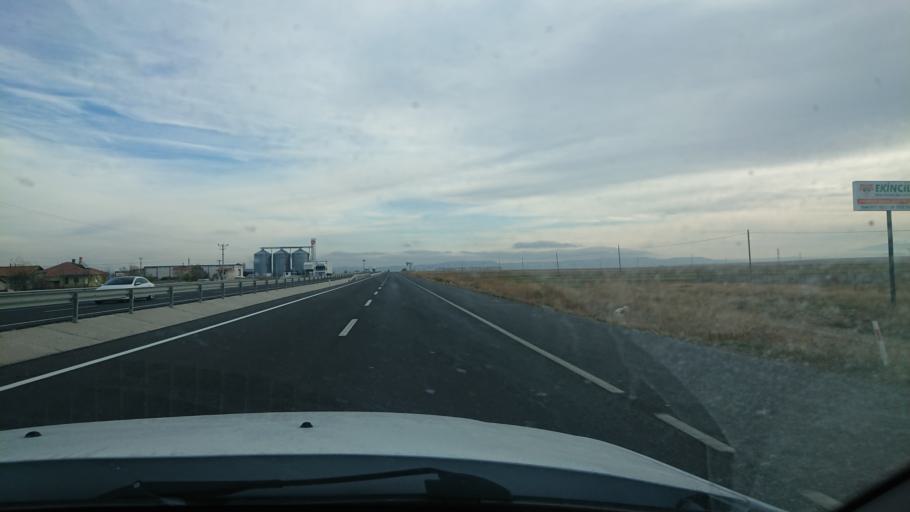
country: TR
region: Aksaray
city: Yesilova
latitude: 38.3266
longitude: 33.8892
